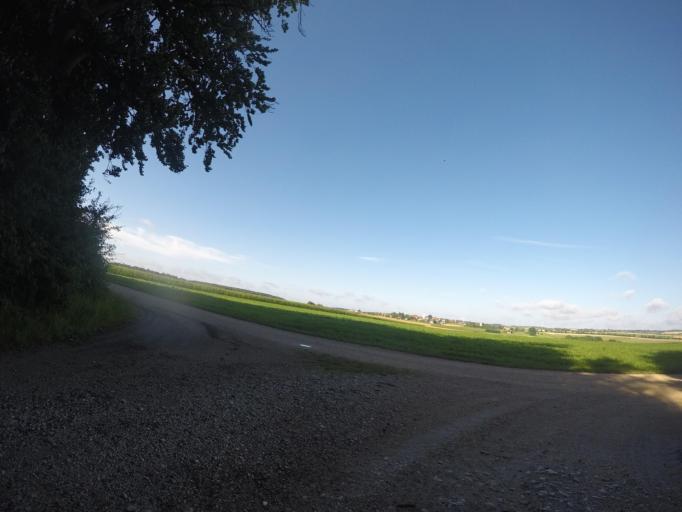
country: DE
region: Baden-Wuerttemberg
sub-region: Tuebingen Region
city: Schelklingen
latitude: 48.3912
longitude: 9.6811
